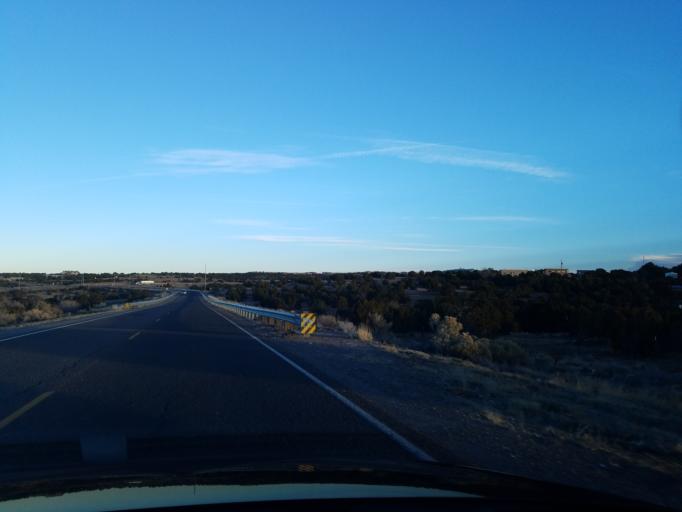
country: US
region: New Mexico
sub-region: Santa Fe County
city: Agua Fria
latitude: 35.6721
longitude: -106.0101
